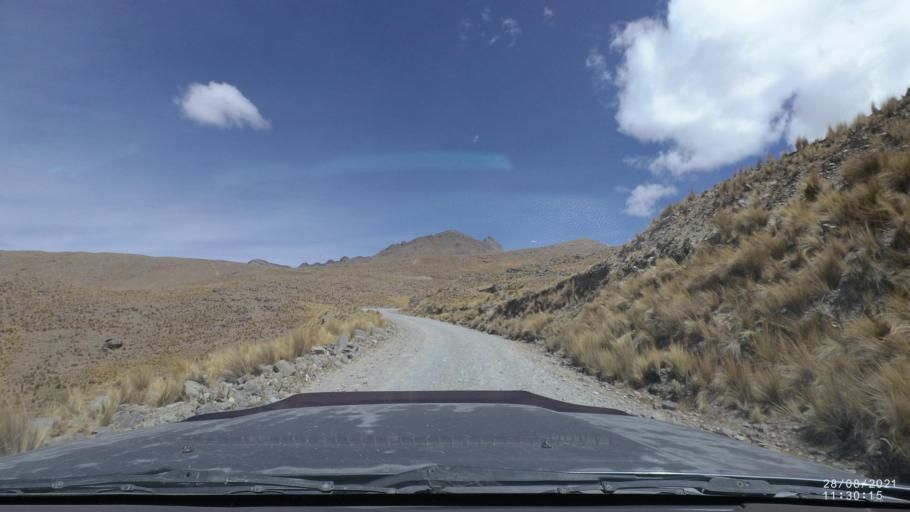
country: BO
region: Cochabamba
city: Sipe Sipe
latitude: -17.1807
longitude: -66.3620
